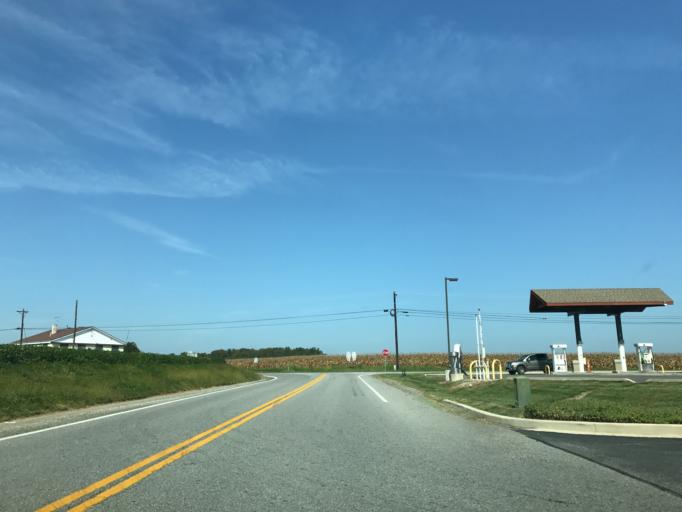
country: US
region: Maryland
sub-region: Queen Anne's County
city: Kingstown
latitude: 39.3195
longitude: -75.9766
